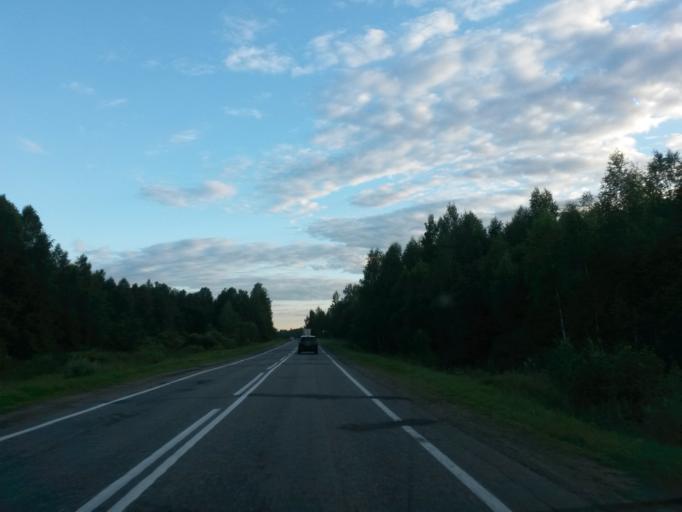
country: RU
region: Jaroslavl
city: Gavrilov-Yam
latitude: 57.3921
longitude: 39.9161
